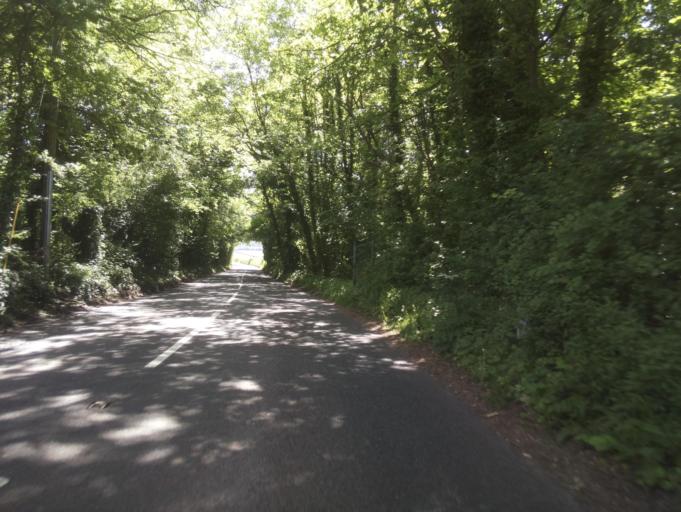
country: GB
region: Wales
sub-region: Monmouthshire
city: Monmouth
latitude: 51.7997
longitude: -2.7190
